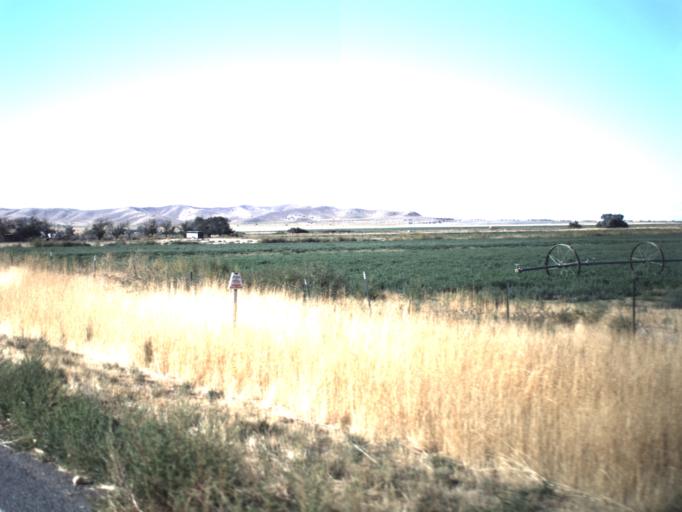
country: US
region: Utah
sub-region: Millard County
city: Delta
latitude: 39.4805
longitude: -112.2688
